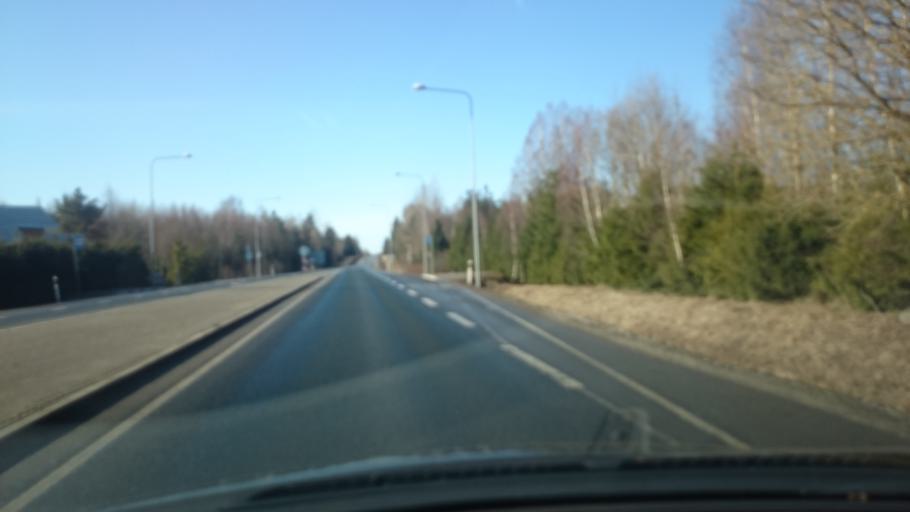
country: EE
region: Raplamaa
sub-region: Rapla vald
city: Rapla
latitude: 59.0396
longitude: 24.8361
